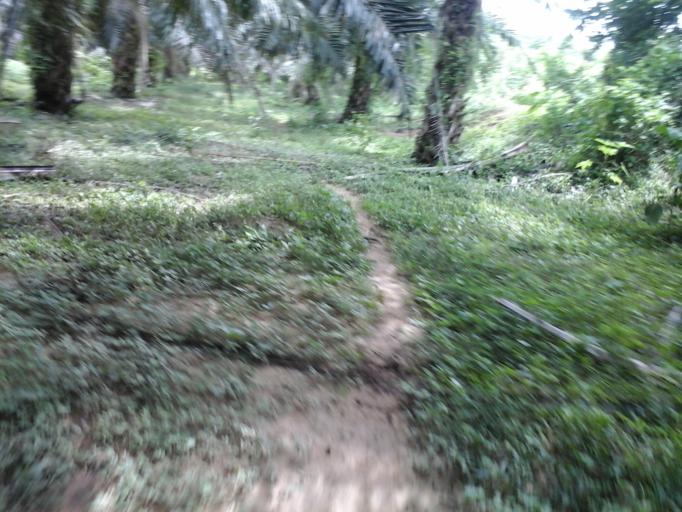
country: CO
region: Bolivar
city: San Pablo
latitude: 10.1575
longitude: -75.2745
